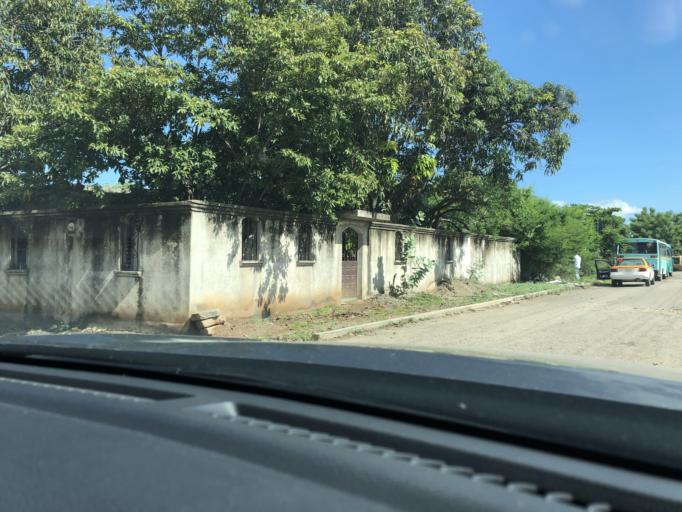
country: MX
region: Oaxaca
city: San Jeronimo Ixtepec
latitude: 16.5565
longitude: -95.1039
